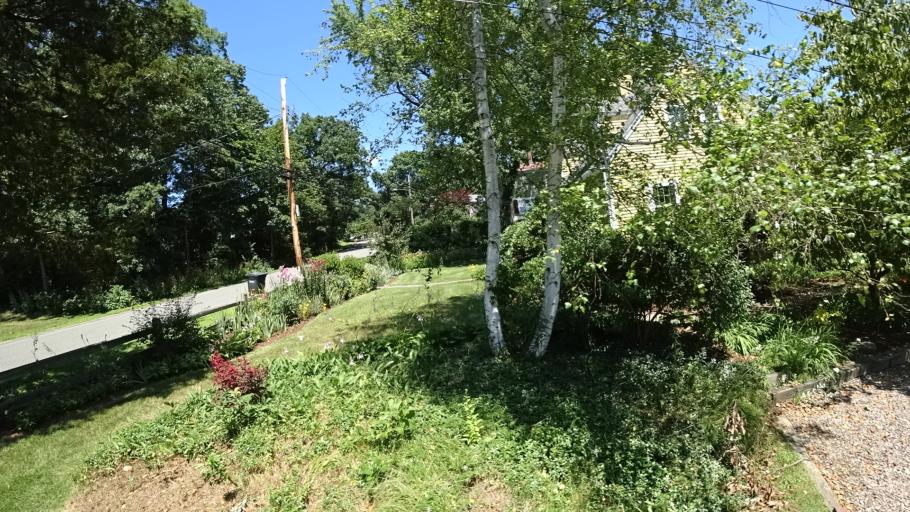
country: US
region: Massachusetts
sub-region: Norfolk County
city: Dedham
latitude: 42.2384
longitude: -71.1838
